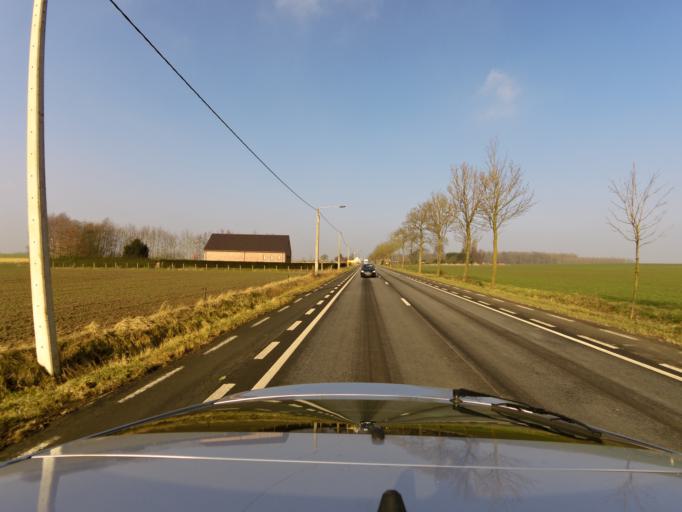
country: BE
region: Wallonia
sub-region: Province du Hainaut
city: Peruwelz
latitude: 50.5596
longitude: 3.5844
